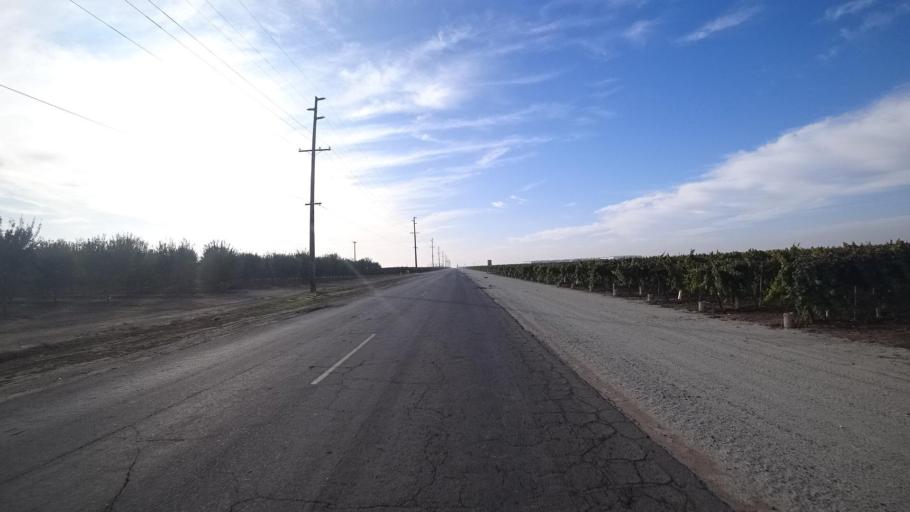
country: US
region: California
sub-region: Kern County
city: McFarland
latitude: 35.7116
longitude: -119.2050
